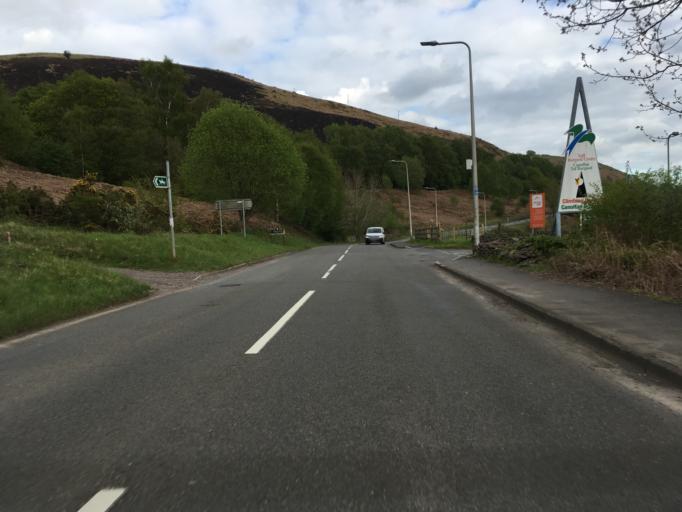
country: GB
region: Wales
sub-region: Merthyr Tydfil County Borough
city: Treharris
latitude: 51.6902
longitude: -3.3002
